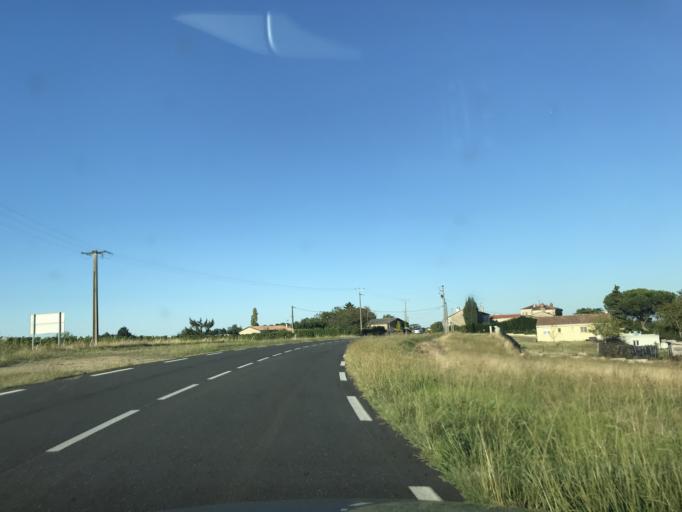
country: FR
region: Aquitaine
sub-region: Departement de la Gironde
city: Saint-Macaire
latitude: 44.5996
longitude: -0.1983
